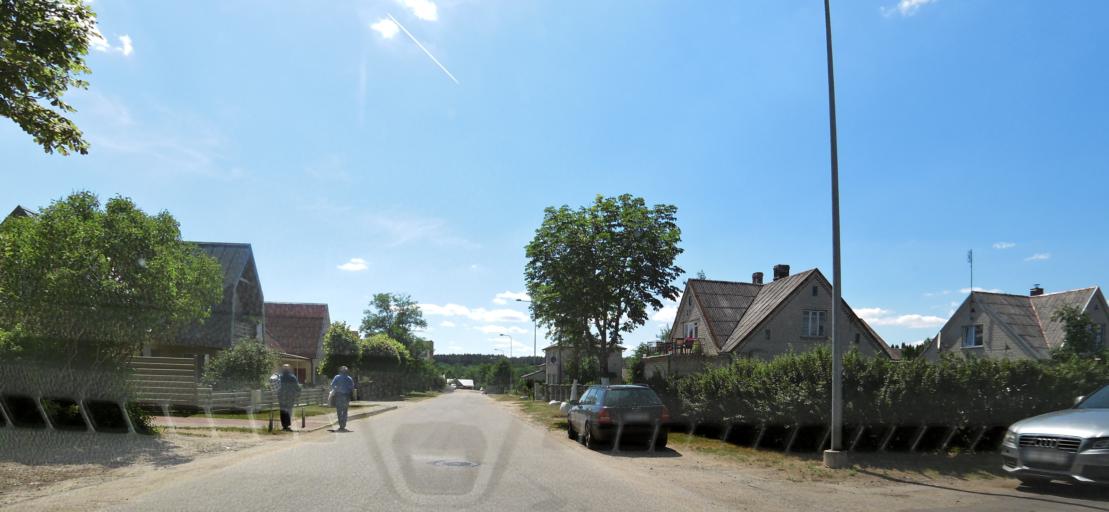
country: LT
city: Nemencine
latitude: 54.8499
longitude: 25.4664
